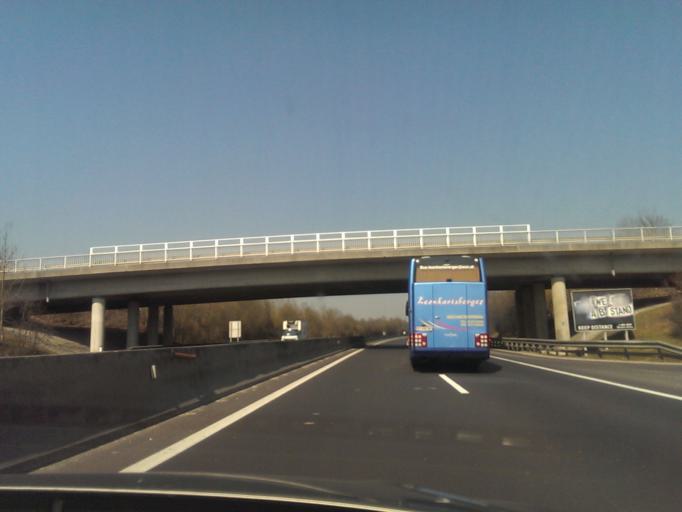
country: AT
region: Upper Austria
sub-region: Wels-Land
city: Gunskirchen
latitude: 48.1554
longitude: 13.9797
